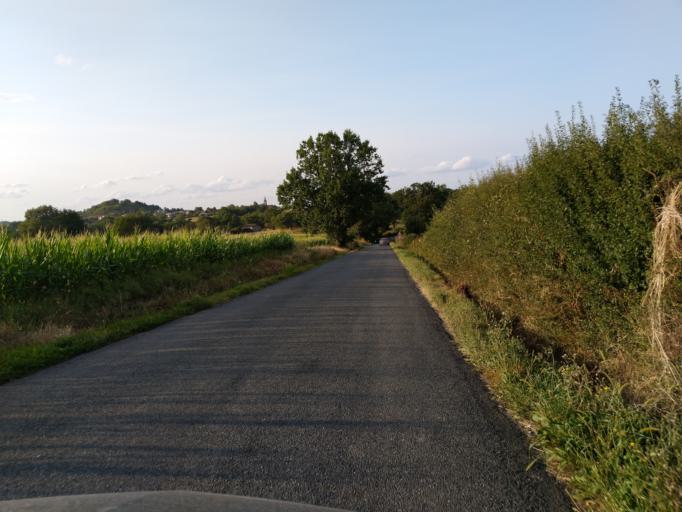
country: FR
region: Midi-Pyrenees
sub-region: Departement du Tarn
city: Frejairolles
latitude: 43.8709
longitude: 2.2336
